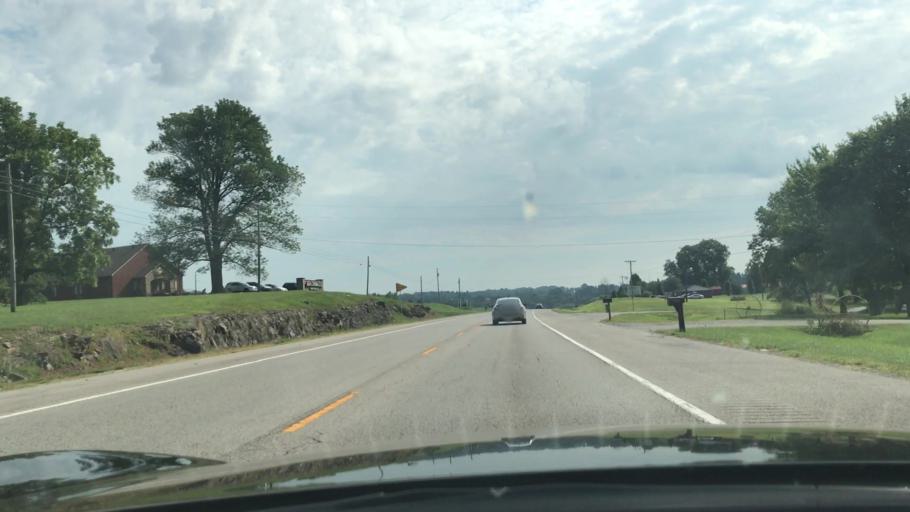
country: US
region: Kentucky
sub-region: Green County
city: Greensburg
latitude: 37.2903
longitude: -85.4763
